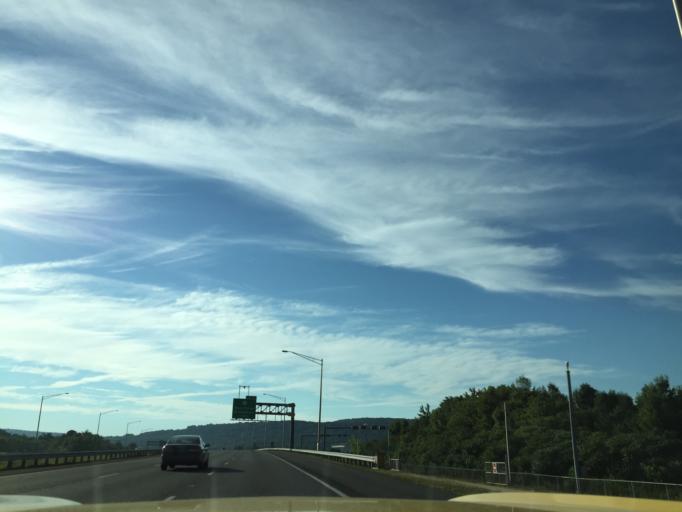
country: US
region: New Jersey
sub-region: Warren County
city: Alpha
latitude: 40.6643
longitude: -75.0899
